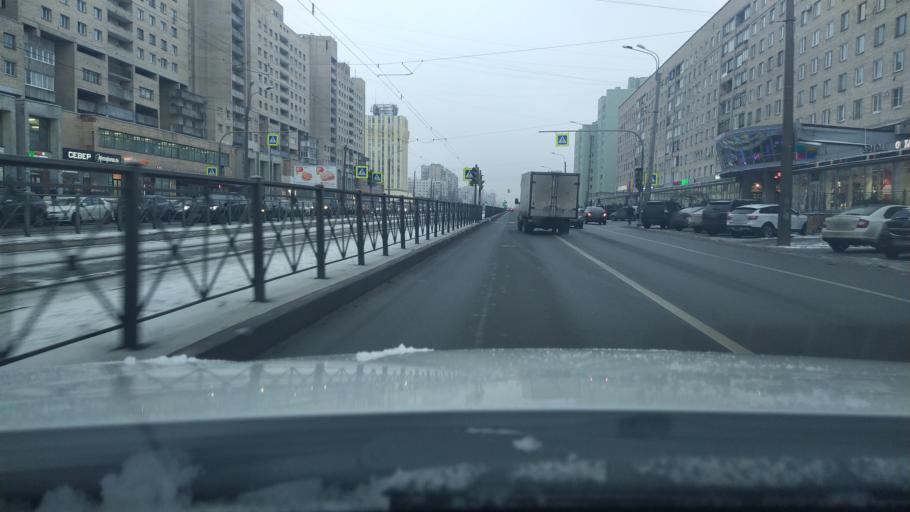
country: RU
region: St.-Petersburg
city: Grazhdanka
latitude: 60.0363
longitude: 30.4163
